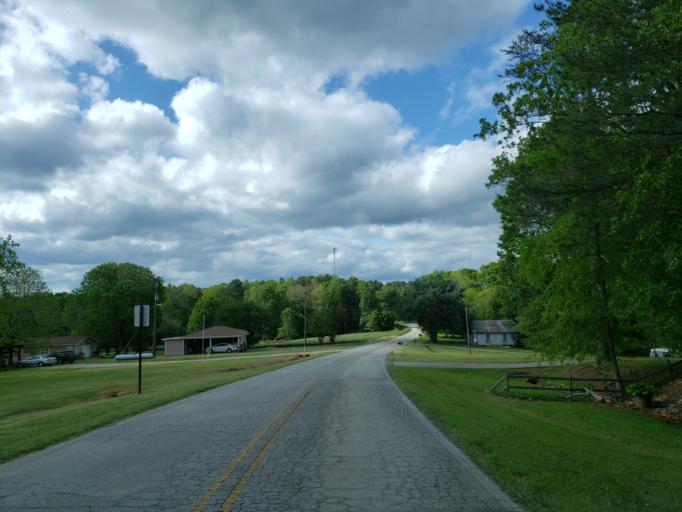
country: US
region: Georgia
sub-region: Haralson County
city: Tallapoosa
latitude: 33.6641
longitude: -85.2837
